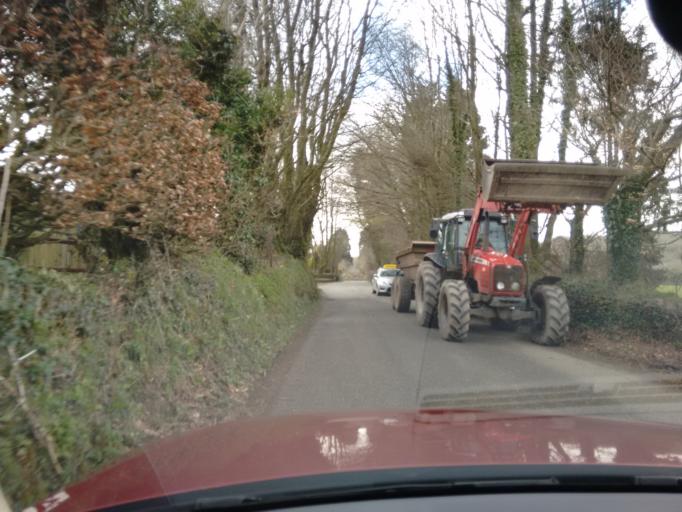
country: GB
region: England
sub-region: Cornwall
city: Liskeard
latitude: 50.4916
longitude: -4.4964
